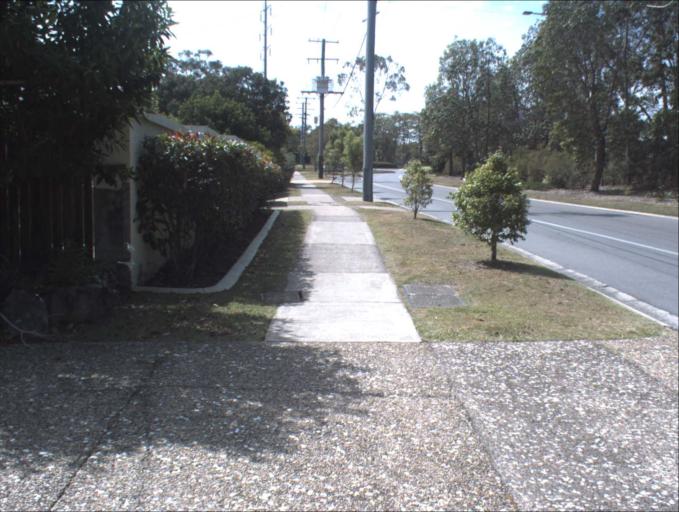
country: AU
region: Queensland
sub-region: Logan
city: Springwood
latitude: -27.6186
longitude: 153.1405
